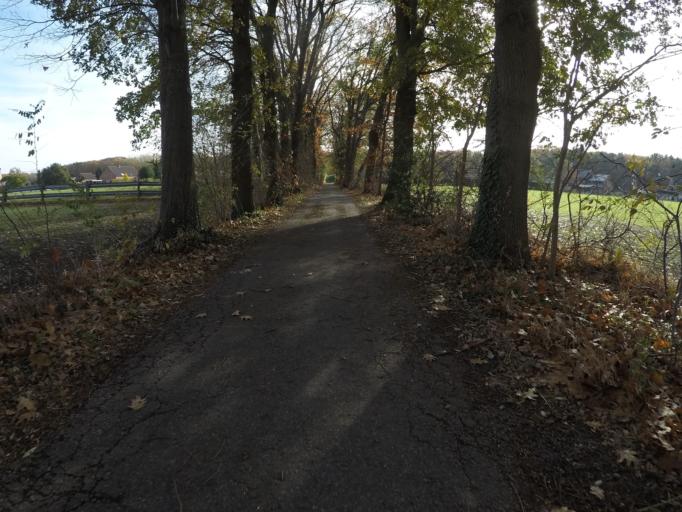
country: BE
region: Flanders
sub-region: Provincie Vlaams-Brabant
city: Begijnendijk
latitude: 51.0290
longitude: 4.7803
